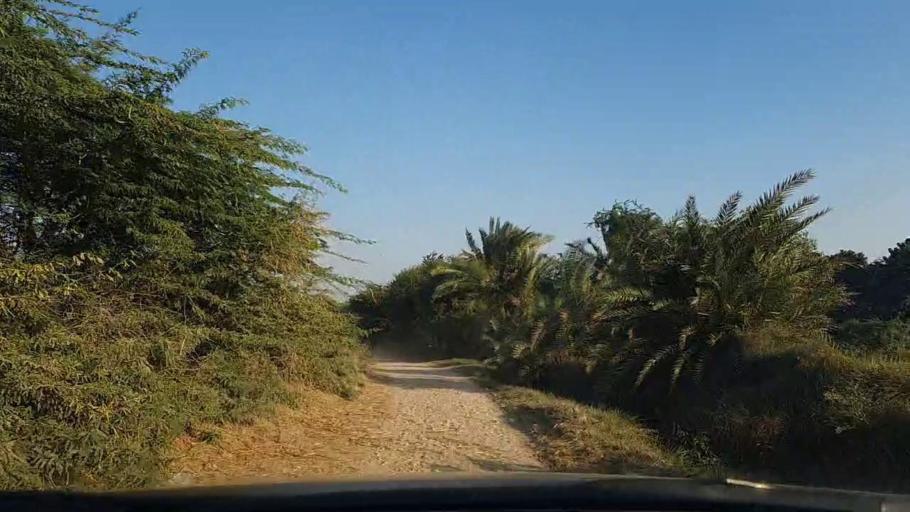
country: PK
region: Sindh
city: Mirpur Sakro
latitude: 24.5212
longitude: 67.6411
